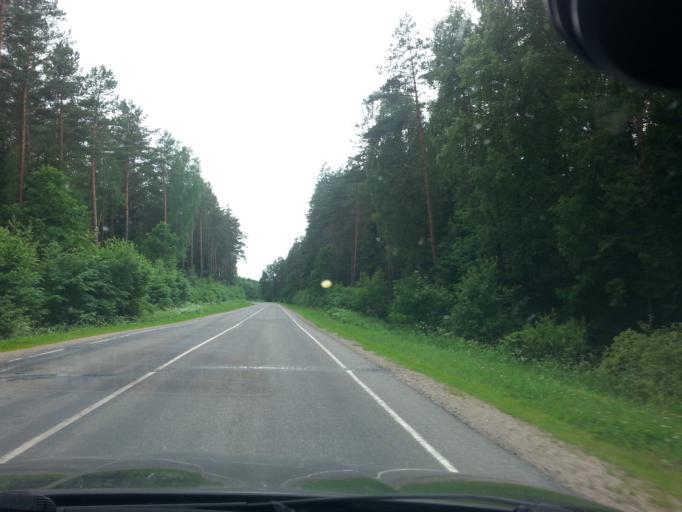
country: BY
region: Minsk
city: Svir
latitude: 54.8378
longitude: 26.1975
